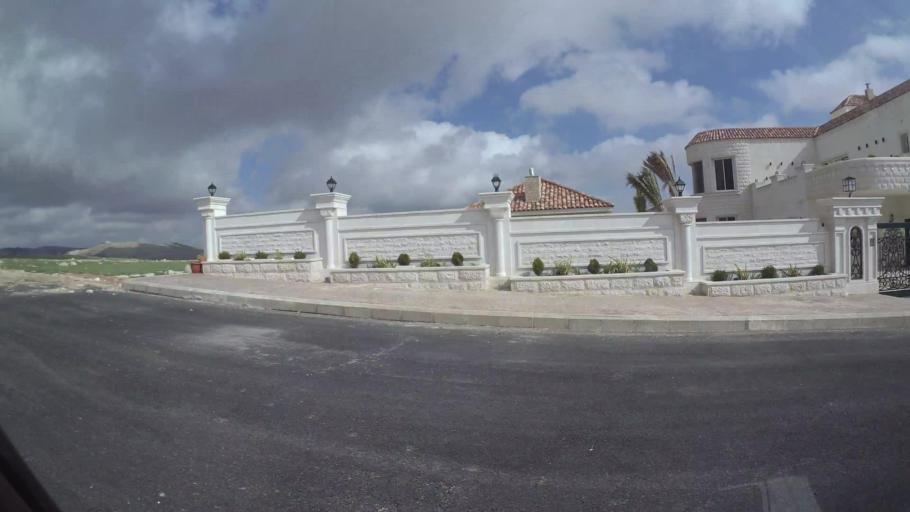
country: JO
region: Amman
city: Al Jubayhah
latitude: 32.0775
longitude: 35.8842
